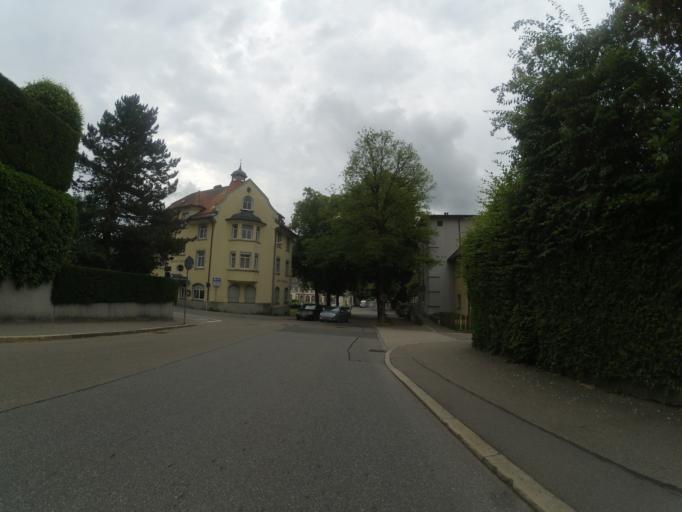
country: DE
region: Baden-Wuerttemberg
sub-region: Tuebingen Region
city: Wangen im Allgau
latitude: 47.6878
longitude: 9.8312
